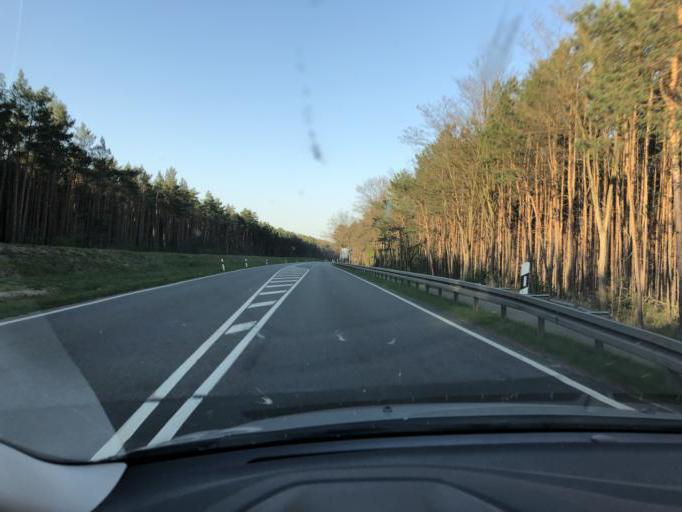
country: DE
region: Brandenburg
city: Schwarzbach
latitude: 51.4806
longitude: 13.9203
